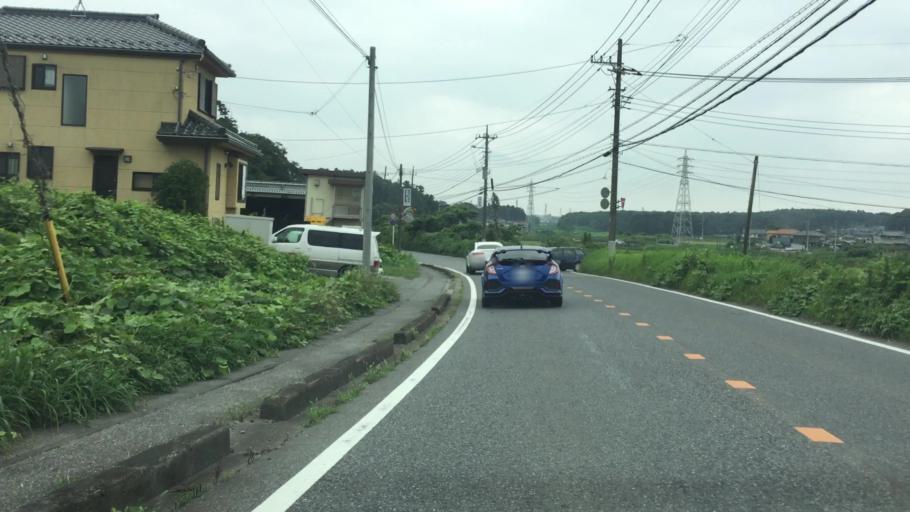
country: JP
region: Chiba
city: Kashiwa
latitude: 35.8266
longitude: 140.0012
